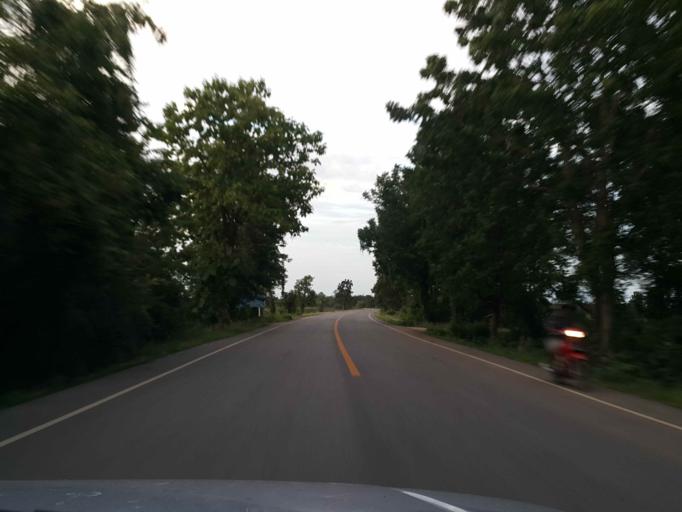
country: TH
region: Sukhothai
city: Ban Dan Lan Hoi
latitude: 17.0762
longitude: 99.5902
